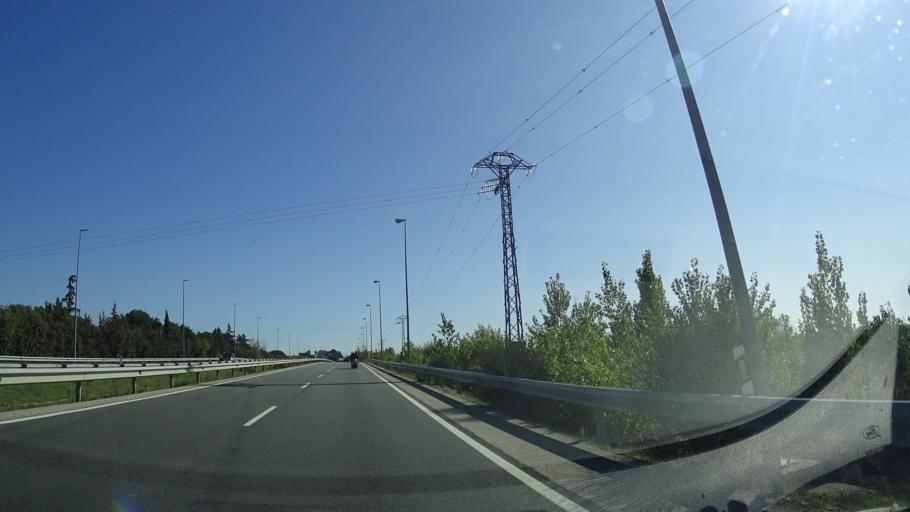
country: ES
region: Madrid
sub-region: Provincia de Madrid
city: Villanueva del Pardillo
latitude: 40.5117
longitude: -3.9252
